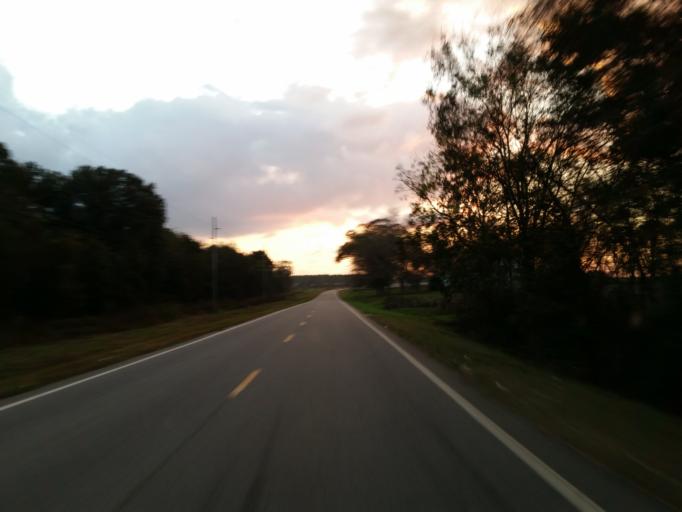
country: US
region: Georgia
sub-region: Dooly County
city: Vienna
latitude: 32.1400
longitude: -83.6807
